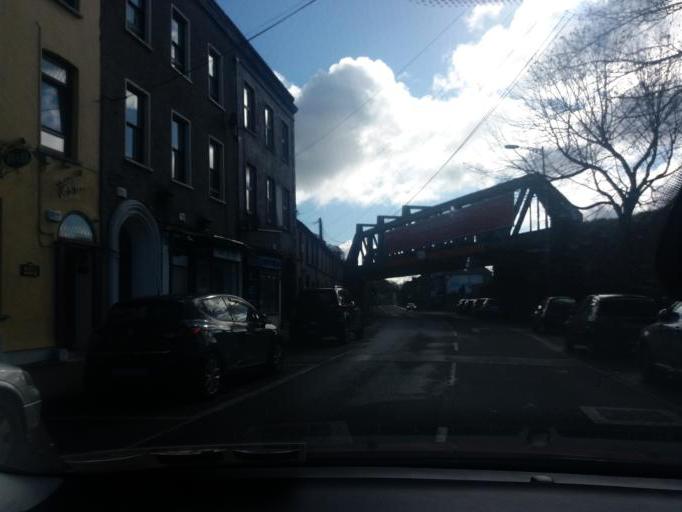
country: IE
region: Munster
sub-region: County Cork
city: Cork
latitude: 51.9027
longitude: -8.4515
